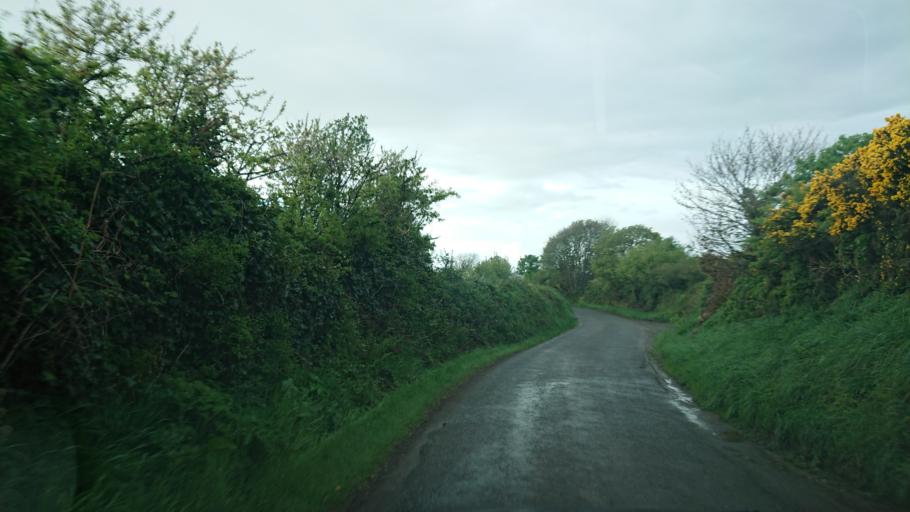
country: IE
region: Munster
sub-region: Waterford
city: Waterford
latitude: 52.2337
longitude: -7.1310
